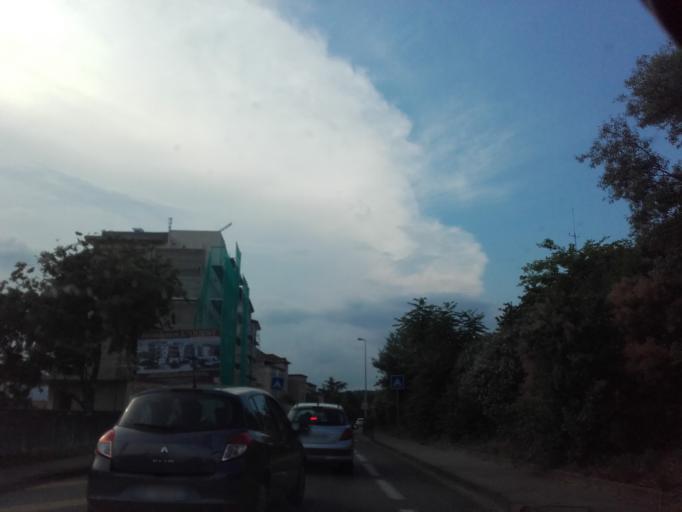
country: FR
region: Rhone-Alpes
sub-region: Departement de l'Isere
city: Le Peage-de-Roussillon
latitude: 45.3752
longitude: 4.8000
